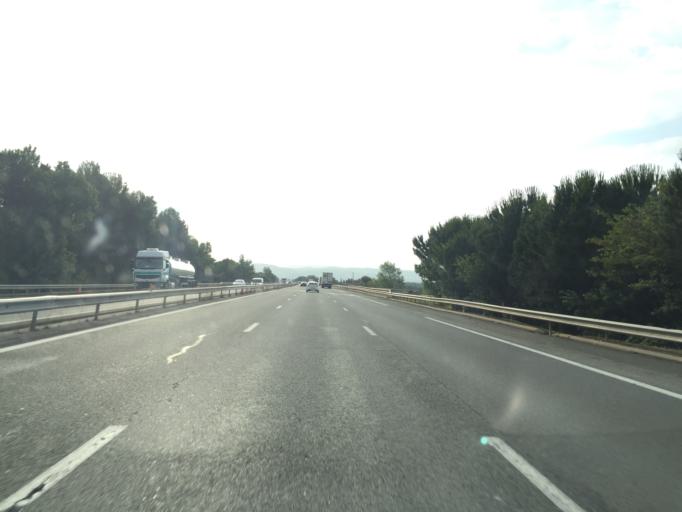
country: FR
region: Provence-Alpes-Cote d'Azur
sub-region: Departement du Var
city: Le Cannet-des-Maures
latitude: 43.4019
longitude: 6.3810
